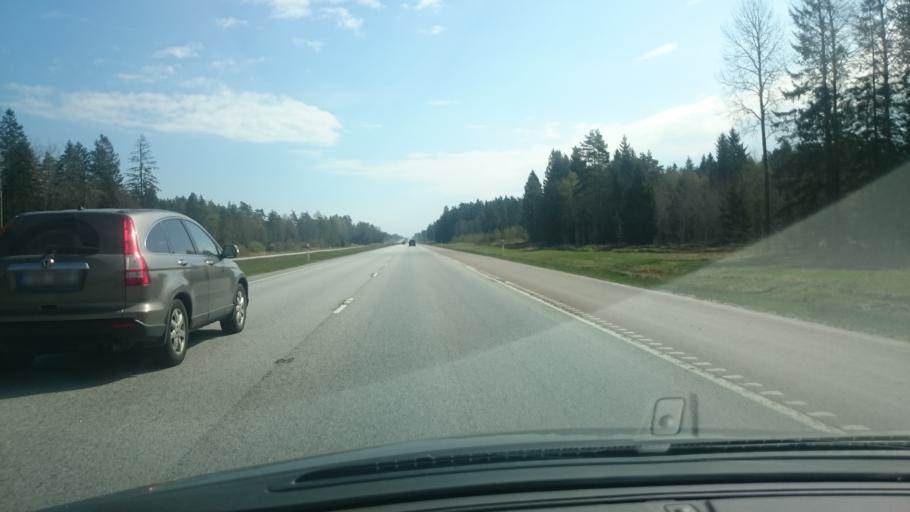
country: EE
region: Harju
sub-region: Raasiku vald
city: Raasiku
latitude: 59.4368
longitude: 25.2288
